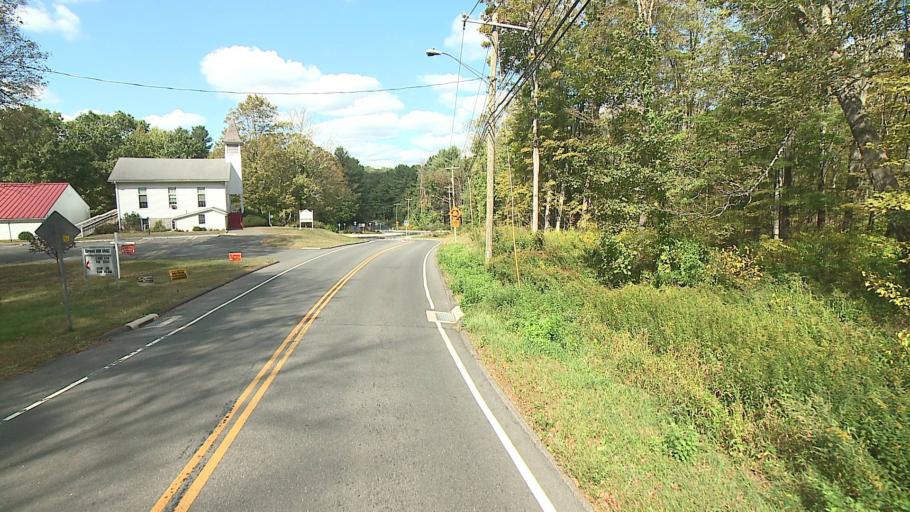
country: US
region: Connecticut
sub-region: New Haven County
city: Seymour
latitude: 41.3774
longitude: -73.1261
